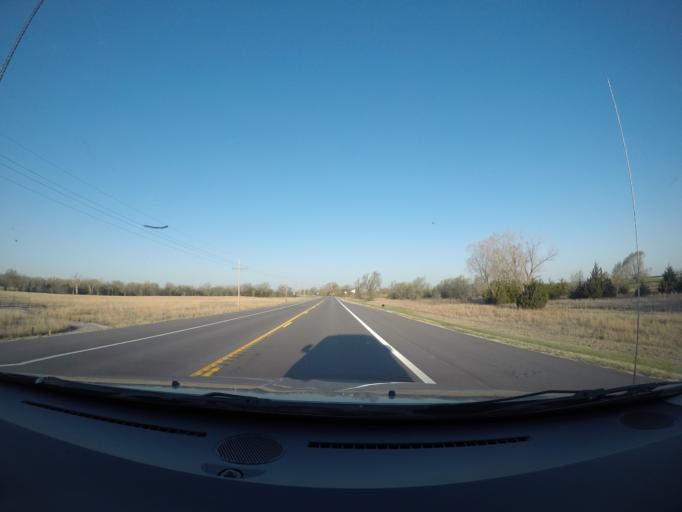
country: US
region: Kansas
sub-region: Stafford County
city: Stafford
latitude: 37.8085
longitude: -98.4341
